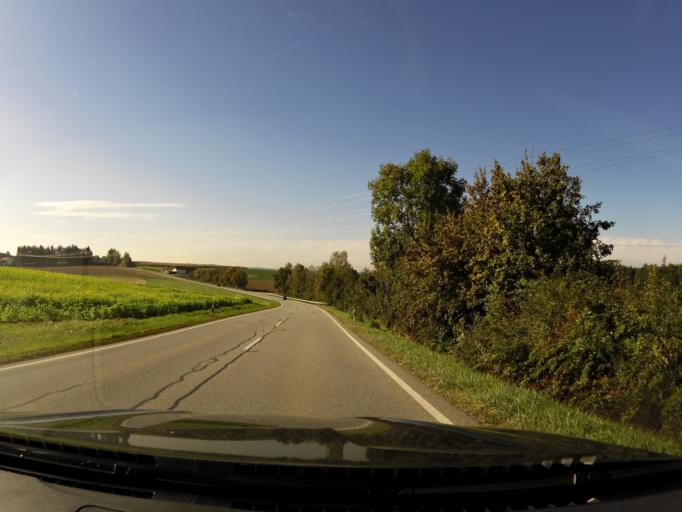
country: DE
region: Bavaria
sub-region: Lower Bavaria
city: Altfraunhofen
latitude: 48.4695
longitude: 12.1545
